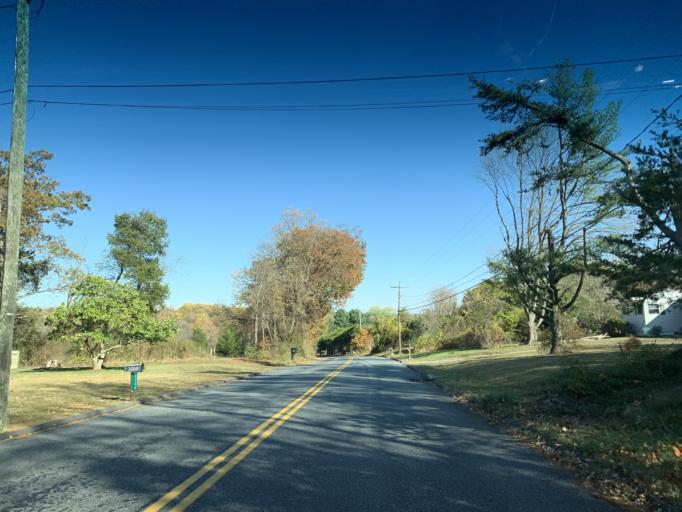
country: US
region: Maryland
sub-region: Harford County
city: Pleasant Hills
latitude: 39.4714
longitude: -76.3733
